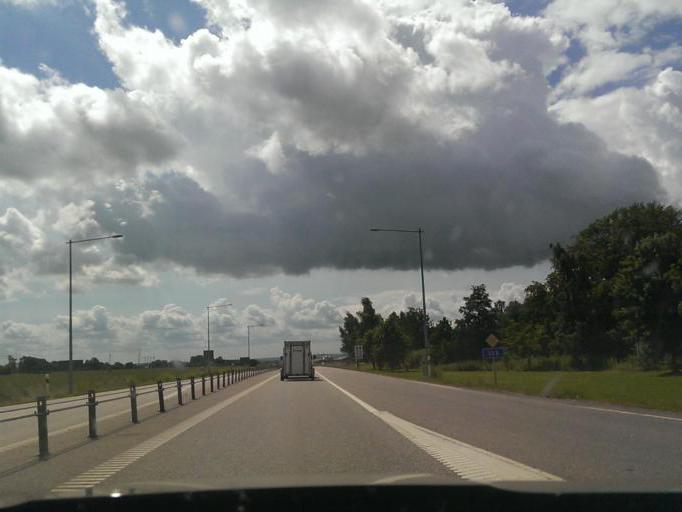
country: SE
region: Skane
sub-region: Eslovs Kommun
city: Eslov
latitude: 55.8358
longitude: 13.3304
